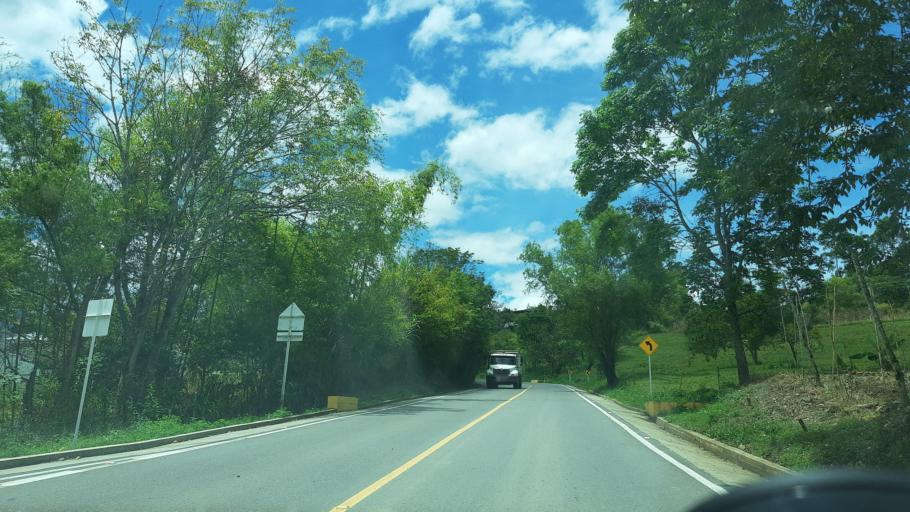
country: CO
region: Boyaca
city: Guateque
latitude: 5.0087
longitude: -73.4517
